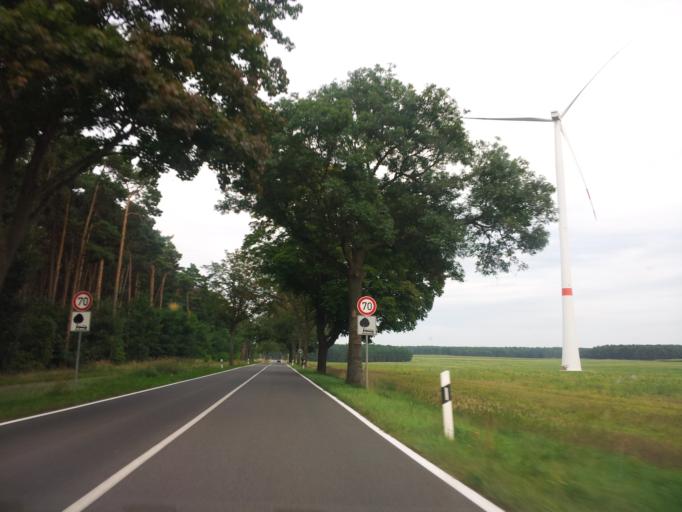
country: DE
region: Brandenburg
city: Linthe
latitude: 52.0954
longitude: 12.7911
